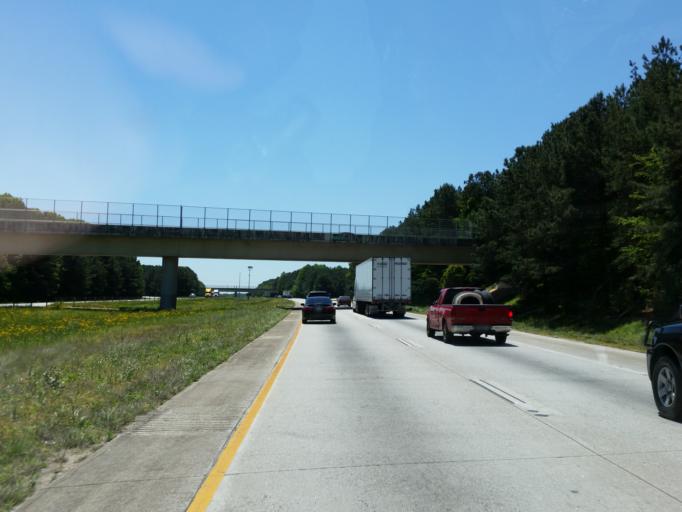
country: US
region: Georgia
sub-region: Clayton County
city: Morrow
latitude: 33.5834
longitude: -84.2806
